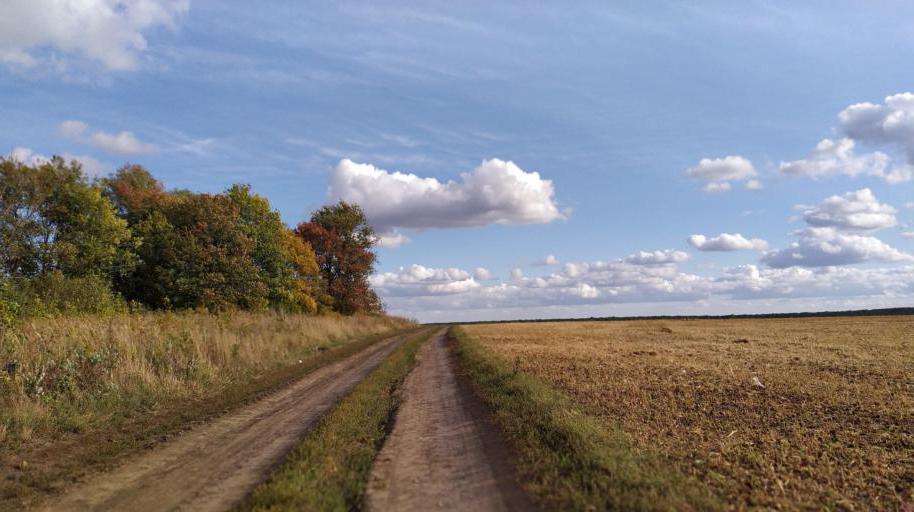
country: RU
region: Kursk
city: Kursk
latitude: 51.6129
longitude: 36.1644
